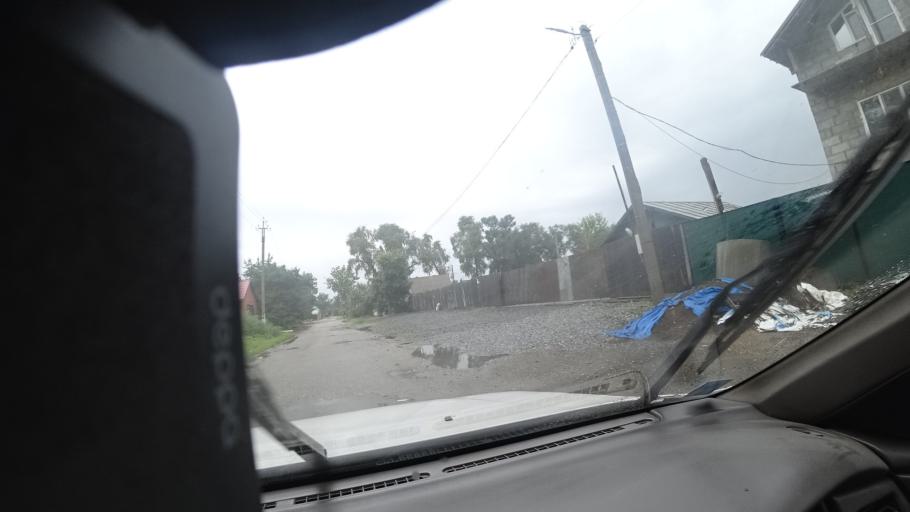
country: RU
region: Primorskiy
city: Dal'nerechensk
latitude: 45.9359
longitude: 133.7396
